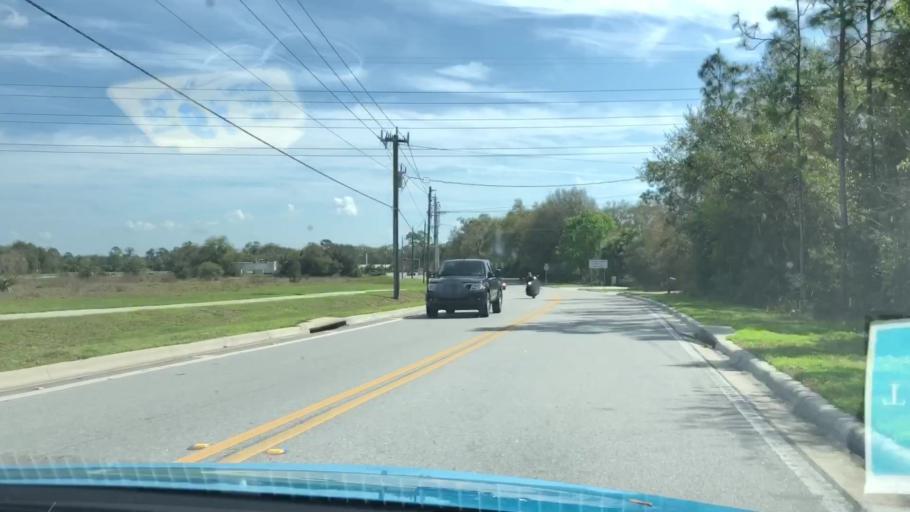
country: US
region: Florida
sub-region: Seminole County
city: Midway
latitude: 28.8505
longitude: -81.1663
